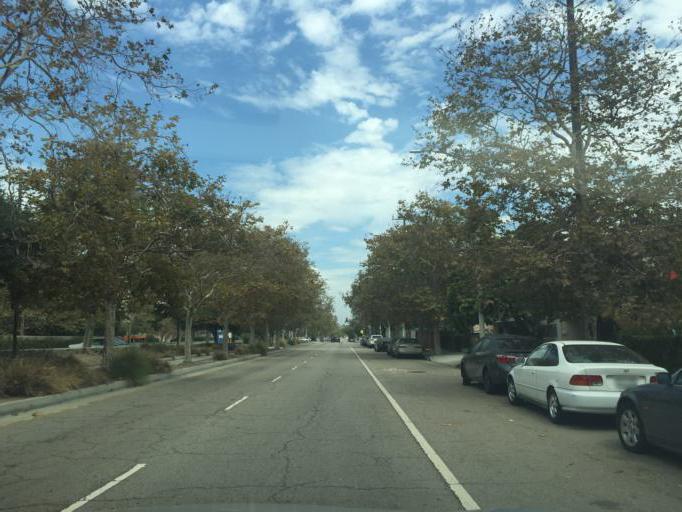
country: US
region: California
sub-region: Los Angeles County
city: Marina del Rey
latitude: 33.9863
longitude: -118.4667
